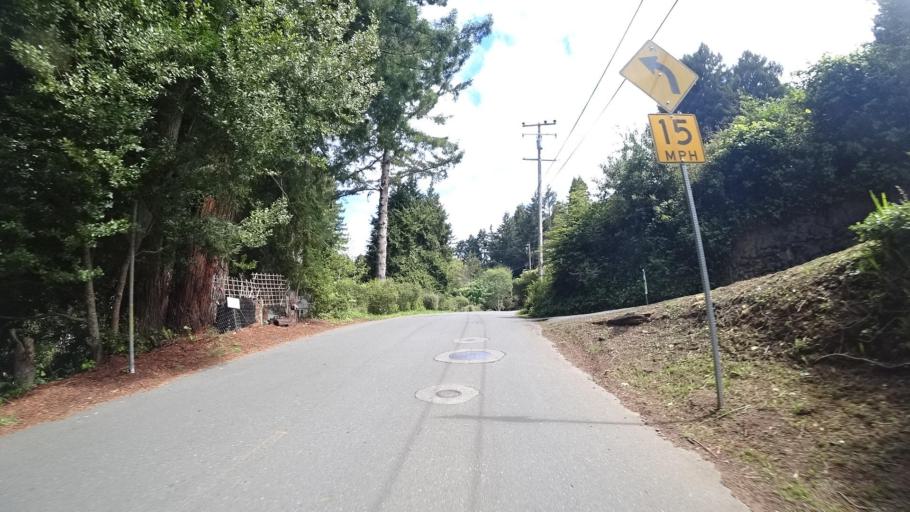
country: US
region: California
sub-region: Humboldt County
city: Arcata
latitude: 40.8658
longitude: -124.0704
